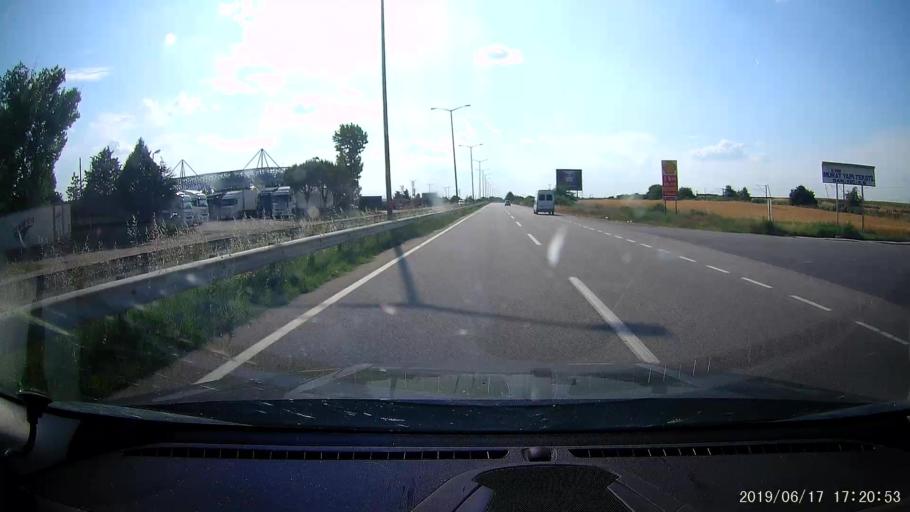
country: GR
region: East Macedonia and Thrace
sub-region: Nomos Evrou
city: Rizia
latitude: 41.7035
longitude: 26.4055
